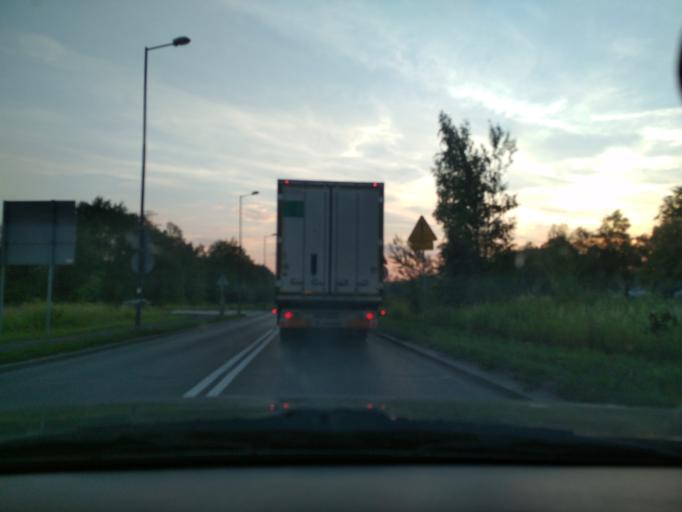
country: PL
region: Silesian Voivodeship
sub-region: Gliwice
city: Gliwice
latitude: 50.2713
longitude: 18.7007
